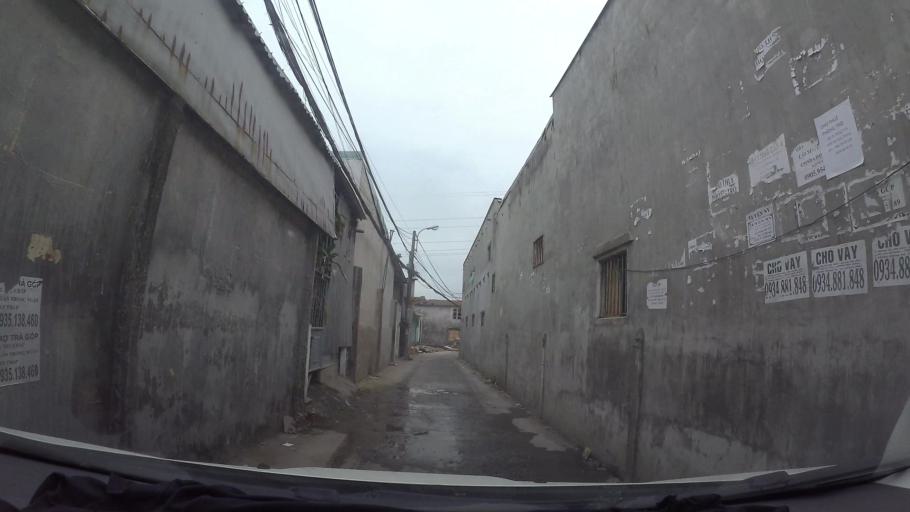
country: VN
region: Da Nang
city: Lien Chieu
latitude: 16.0644
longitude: 108.1515
